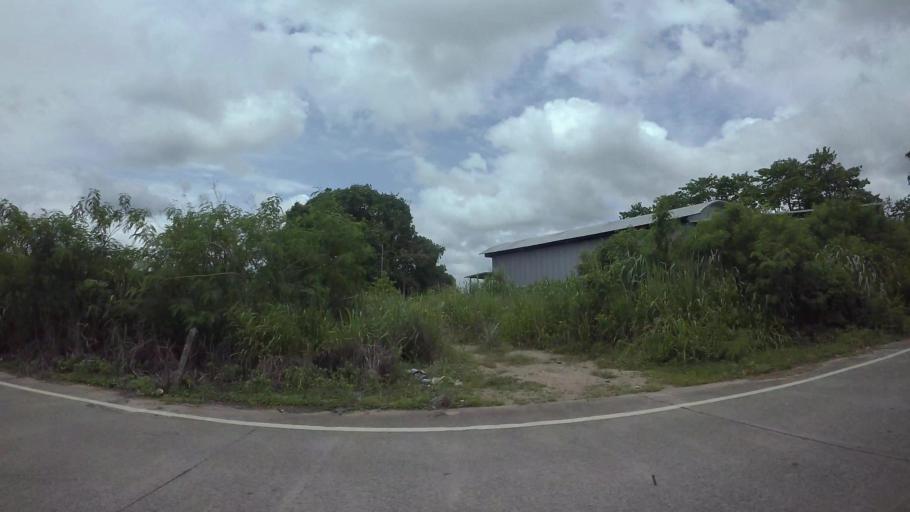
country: TH
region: Chon Buri
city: Si Racha
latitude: 13.1721
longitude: 100.9768
